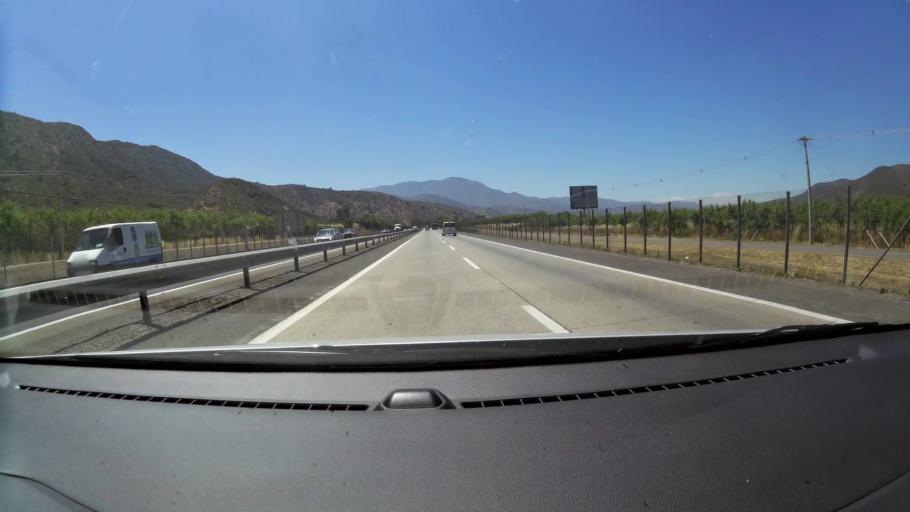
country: CL
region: Santiago Metropolitan
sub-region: Provincia de Chacabuco
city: Lampa
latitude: -33.4012
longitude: -71.1085
